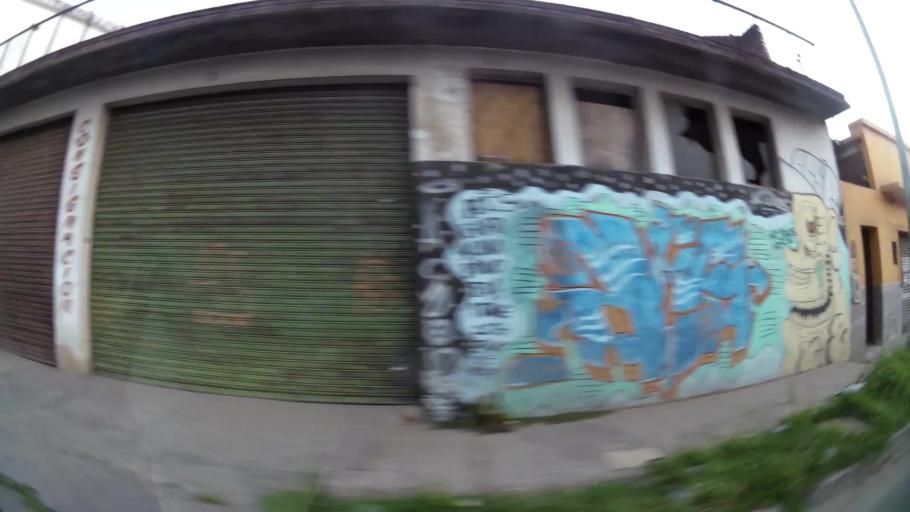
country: AR
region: Buenos Aires
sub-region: Partido de Quilmes
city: Quilmes
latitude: -34.7980
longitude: -58.2827
